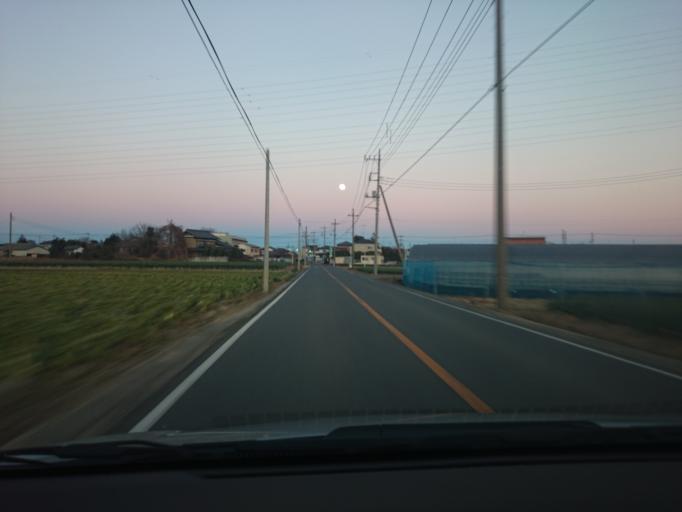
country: JP
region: Saitama
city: Fukayacho
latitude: 36.2284
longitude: 139.2781
